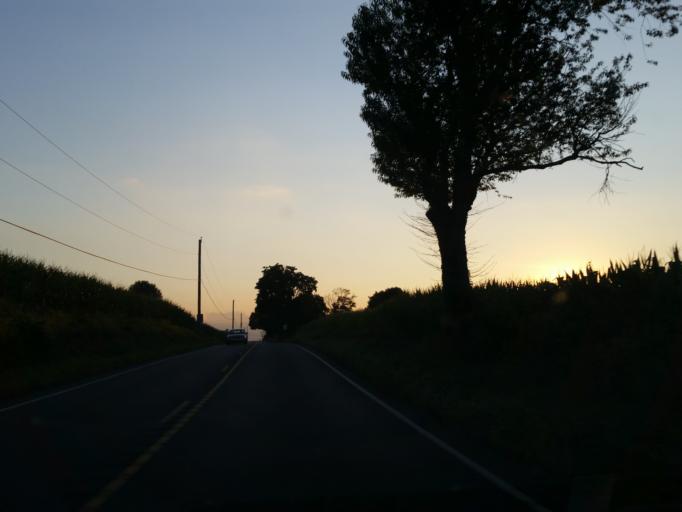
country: US
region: Pennsylvania
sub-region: Lebanon County
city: Cornwall
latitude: 40.2879
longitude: -76.3689
